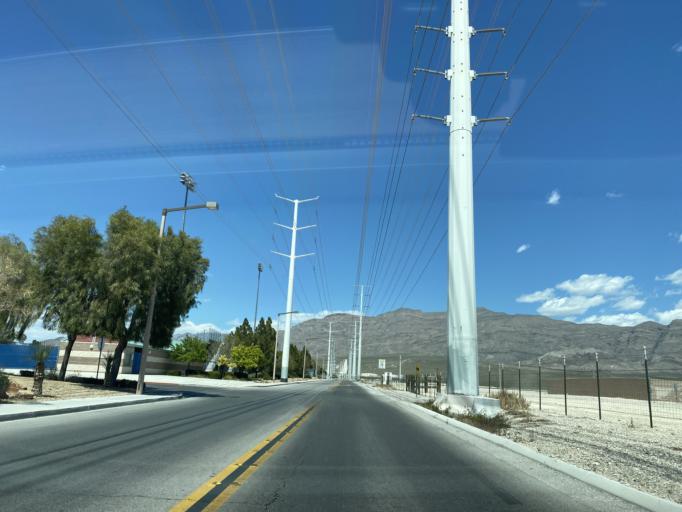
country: US
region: Nevada
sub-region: Clark County
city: North Las Vegas
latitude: 36.3166
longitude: -115.2071
